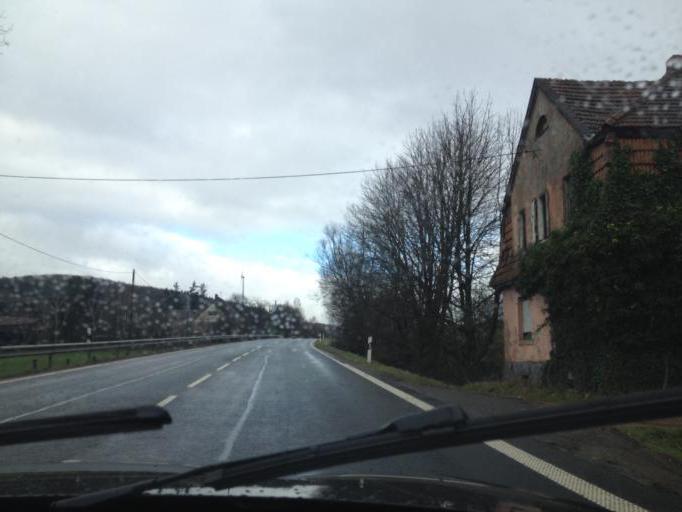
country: DE
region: Rheinland-Pfalz
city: Ellweiler
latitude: 49.6090
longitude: 7.1607
